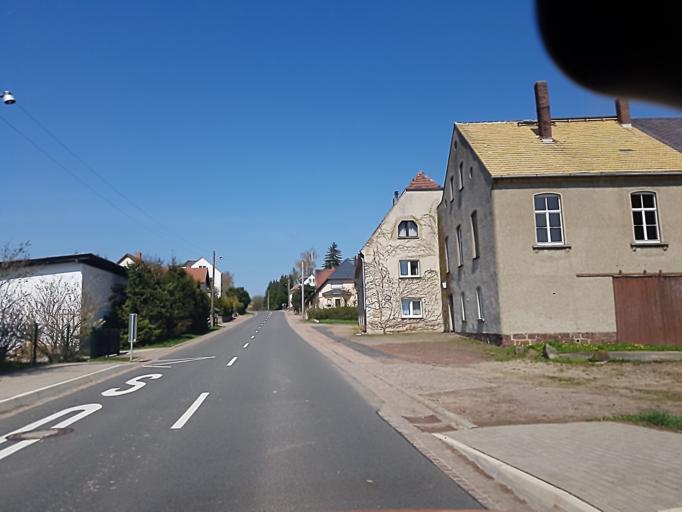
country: DE
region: Saxony
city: Ostrau
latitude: 51.2099
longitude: 12.8921
